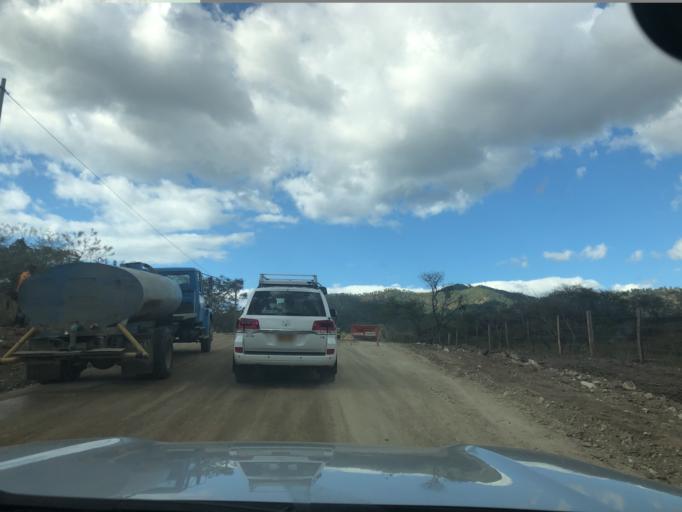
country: NI
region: Nueva Segovia
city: Ocotal
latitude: 13.6592
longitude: -86.6136
